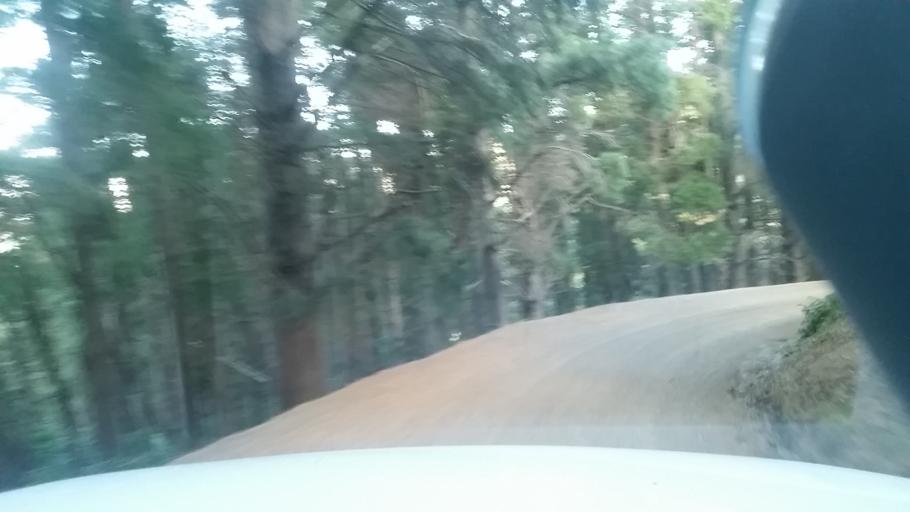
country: NZ
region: Canterbury
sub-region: Christchurch City
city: Christchurch
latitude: -43.7368
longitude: 172.9572
